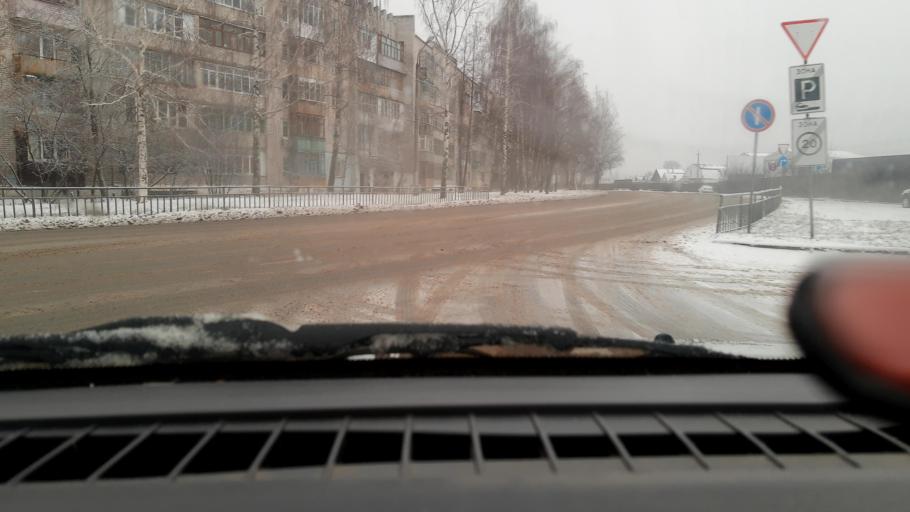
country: RU
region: Nizjnij Novgorod
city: Kstovo
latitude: 56.1455
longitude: 44.1787
